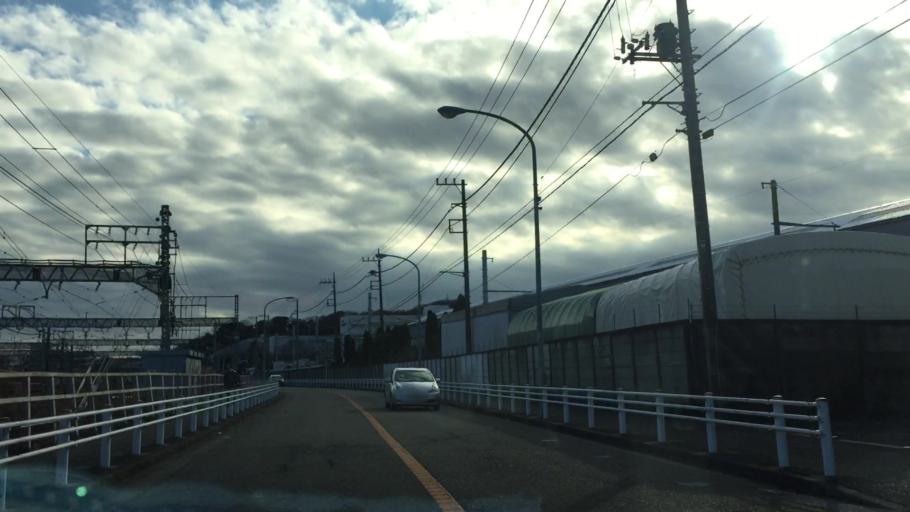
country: JP
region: Kanagawa
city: Zushi
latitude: 35.3375
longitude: 139.6200
